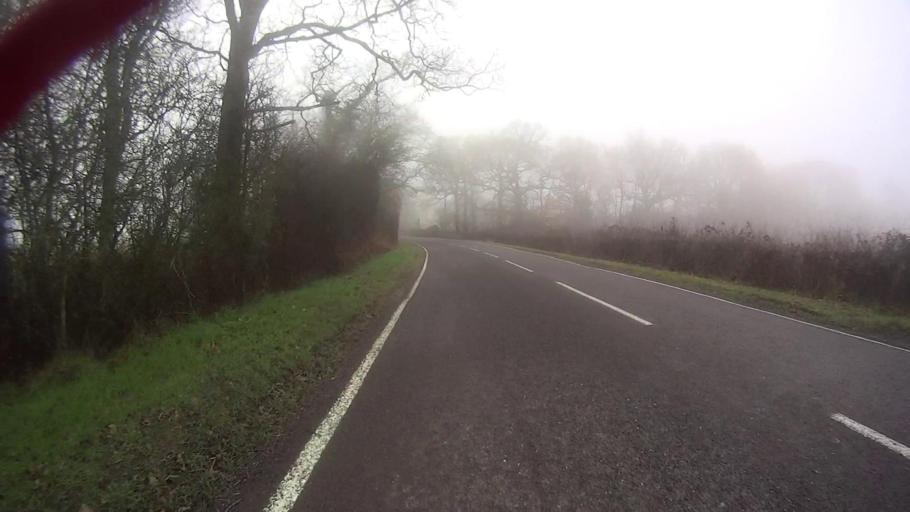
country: GB
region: England
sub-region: Surrey
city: Newdigate
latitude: 51.1416
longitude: -0.3184
